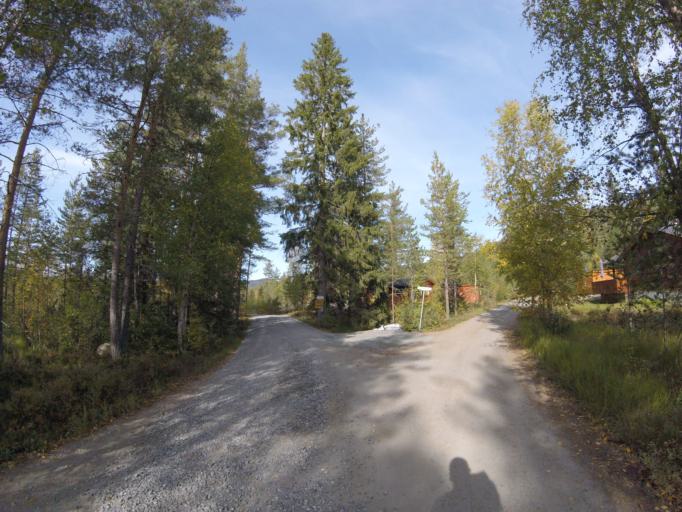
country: NO
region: Buskerud
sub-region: Flesberg
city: Lampeland
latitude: 59.7130
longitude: 9.4075
